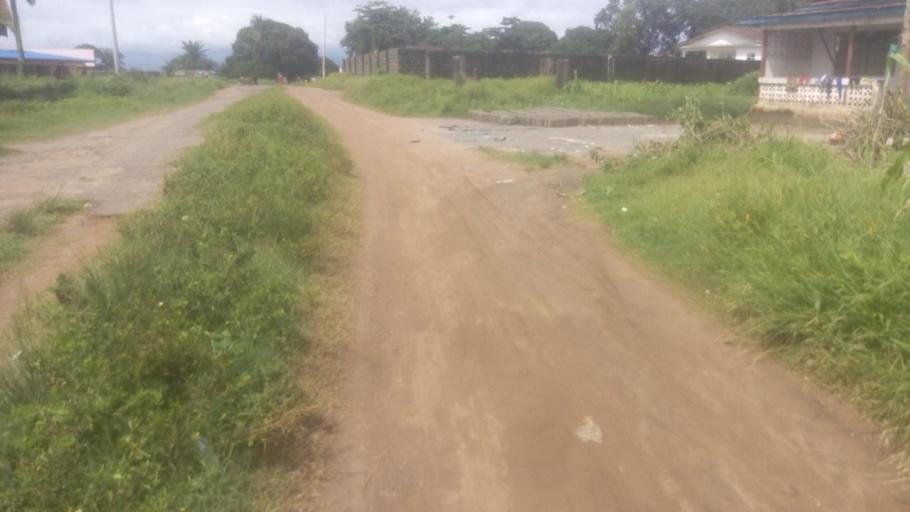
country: SL
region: Northern Province
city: Masoyila
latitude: 8.5879
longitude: -13.1996
